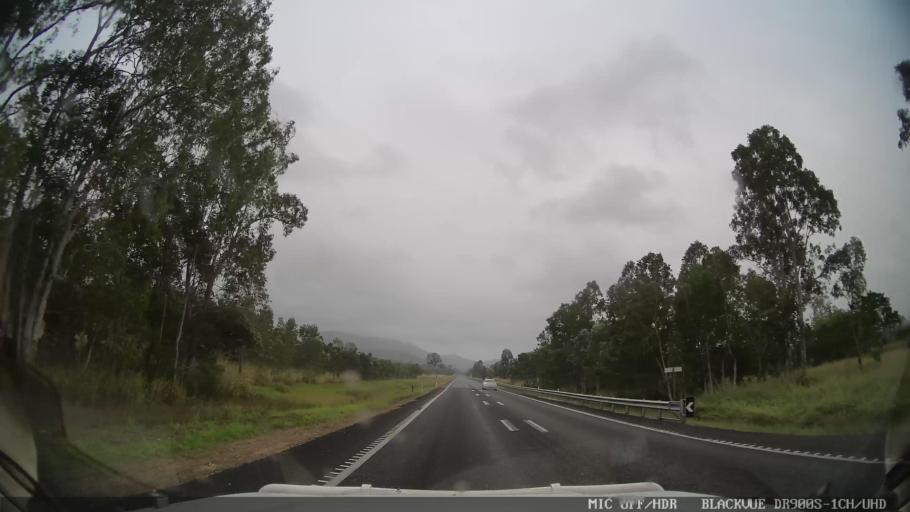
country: AU
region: Queensland
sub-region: Hinchinbrook
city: Ingham
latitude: -18.2100
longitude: 145.9631
